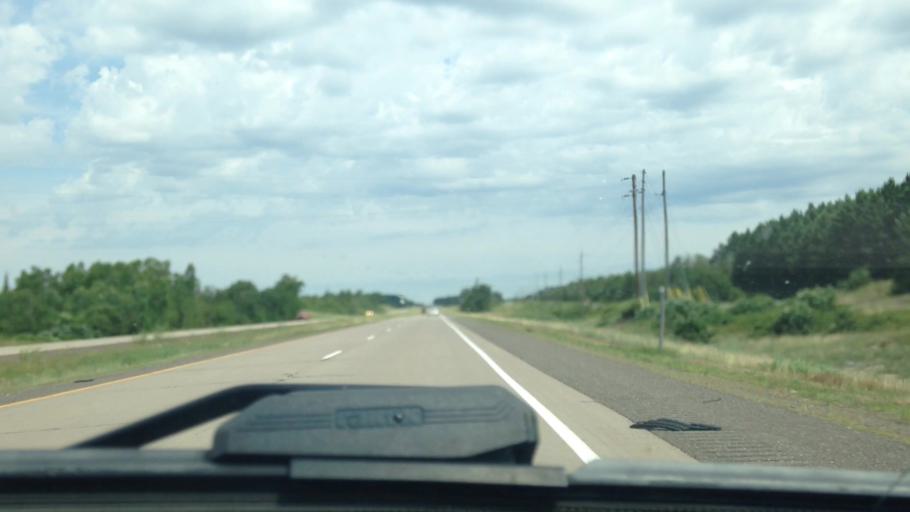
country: US
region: Wisconsin
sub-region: Douglas County
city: Lake Nebagamon
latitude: 46.1881
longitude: -91.7989
